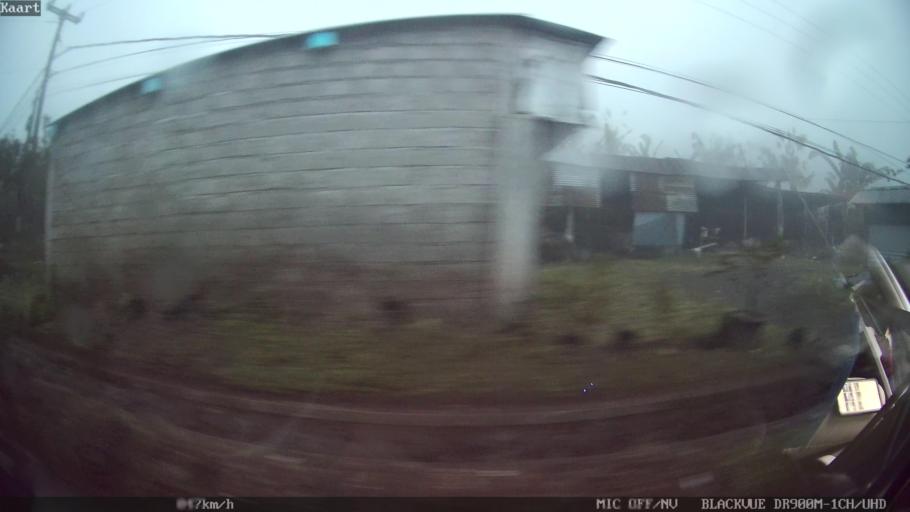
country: ID
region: Bali
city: Banjar Taro Kelod
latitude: -8.3287
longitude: 115.2899
